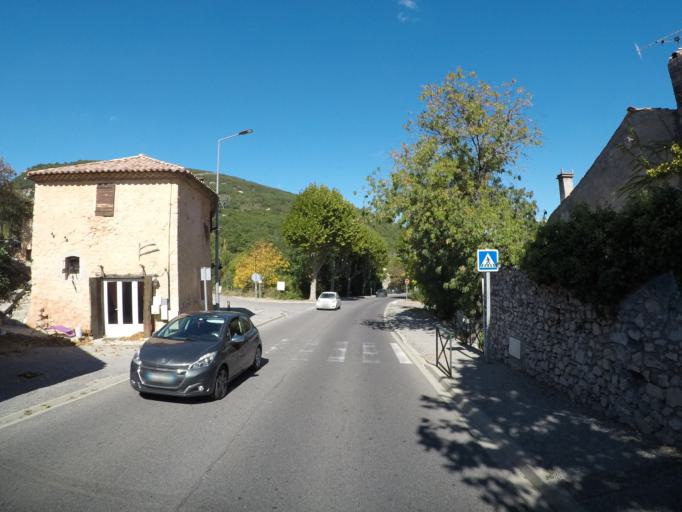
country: FR
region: Provence-Alpes-Cote d'Azur
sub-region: Departement des Alpes-de-Haute-Provence
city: Peipin
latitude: 44.1612
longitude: 5.9502
